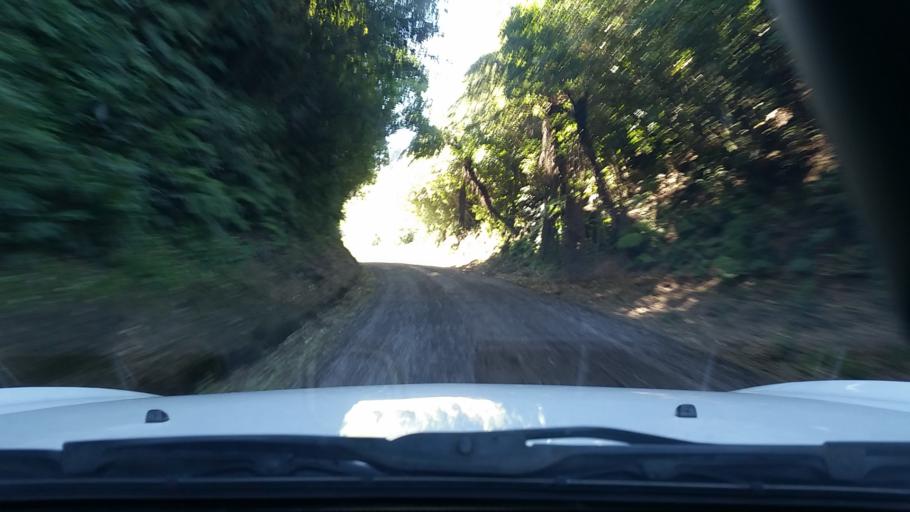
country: NZ
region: Bay of Plenty
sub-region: Rotorua District
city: Rotorua
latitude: -38.3776
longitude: 176.1202
